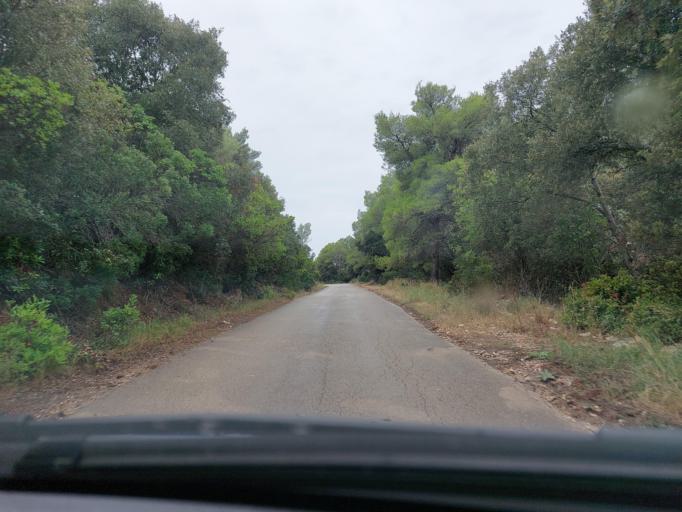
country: HR
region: Dubrovacko-Neretvanska
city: Smokvica
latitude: 42.7447
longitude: 16.8327
